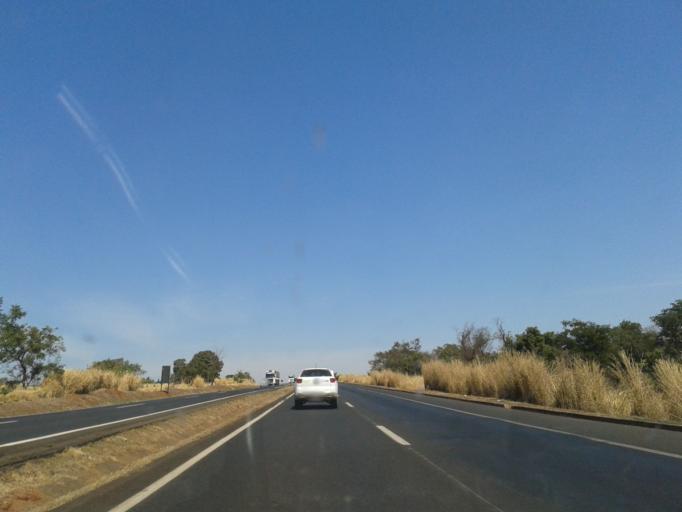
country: BR
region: Minas Gerais
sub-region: Monte Alegre De Minas
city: Monte Alegre de Minas
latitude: -18.8380
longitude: -49.0920
